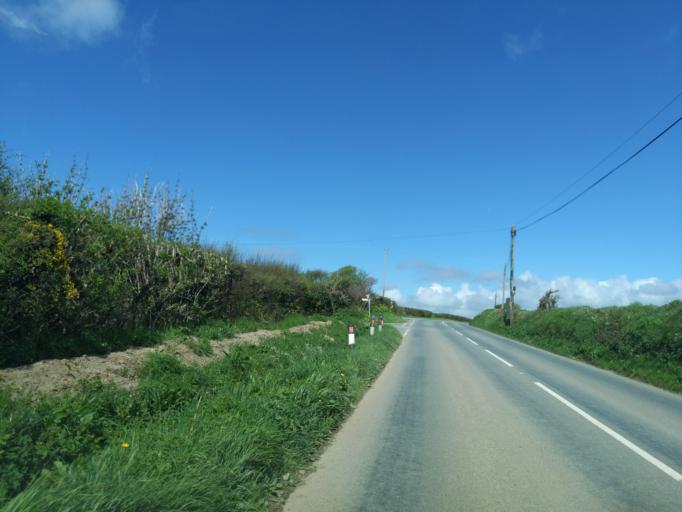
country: GB
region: England
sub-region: Cornwall
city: Wadebridge
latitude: 50.5847
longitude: -4.7855
